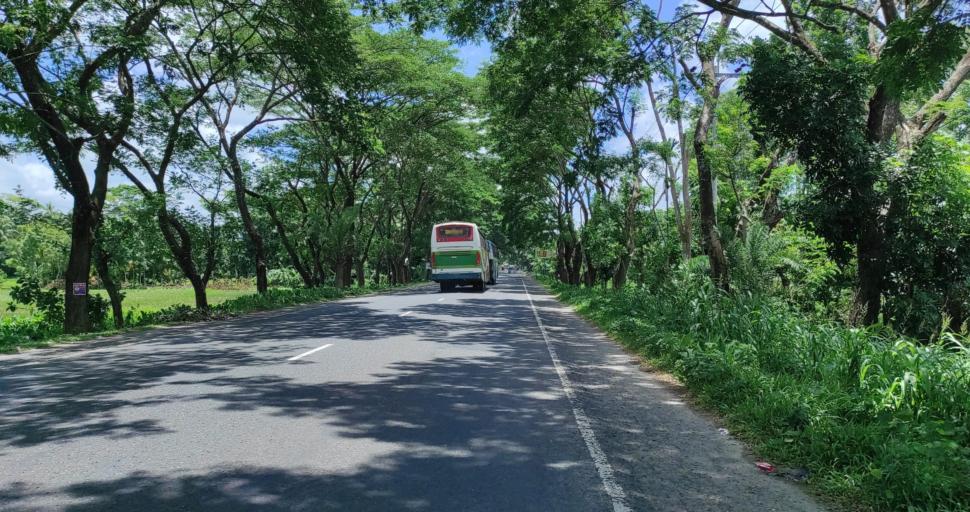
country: BD
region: Barisal
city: Barisal
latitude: 22.8209
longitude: 90.2688
